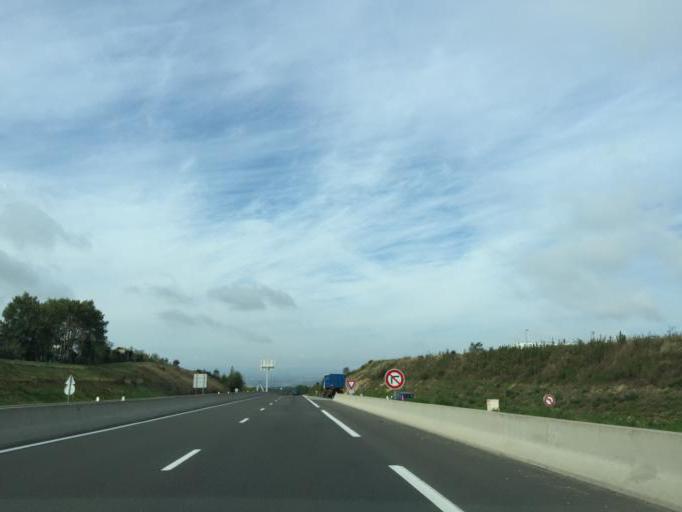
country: FR
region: Rhone-Alpes
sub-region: Departement de la Loire
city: Andrezieux-Boutheon
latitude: 45.5174
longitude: 4.2627
